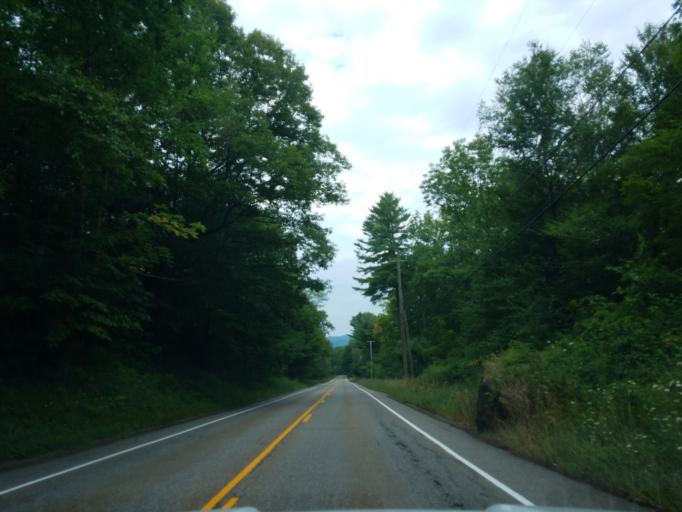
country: US
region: Connecticut
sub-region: Litchfield County
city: New Preston
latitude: 41.7834
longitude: -73.3568
